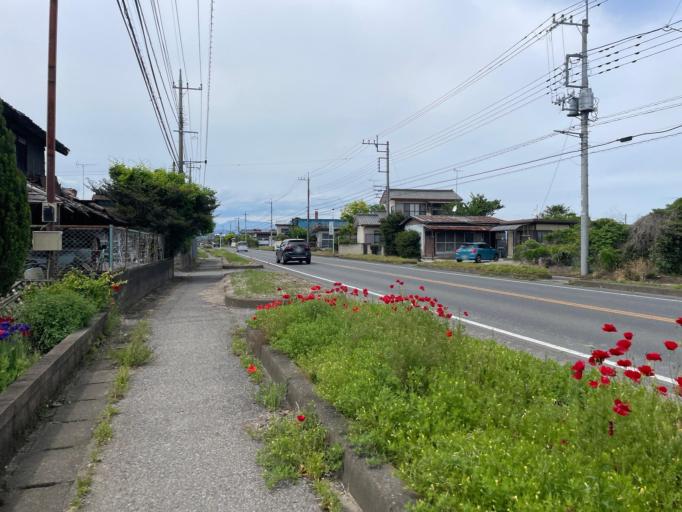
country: JP
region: Tochigi
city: Mibu
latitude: 36.4644
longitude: 139.7682
